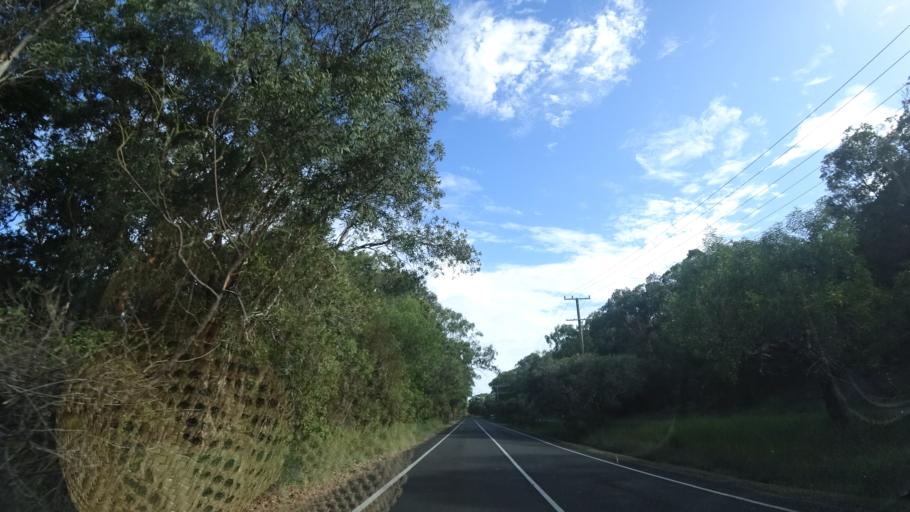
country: AU
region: Queensland
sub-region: Sunshine Coast
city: Coolum Beach
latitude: -26.5597
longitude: 153.0906
